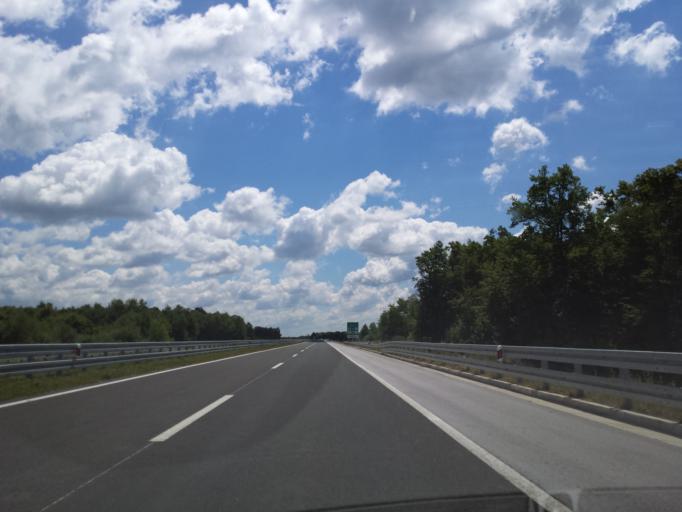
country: HR
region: Zagrebacka
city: Turopolje
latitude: 45.5984
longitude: 16.1416
